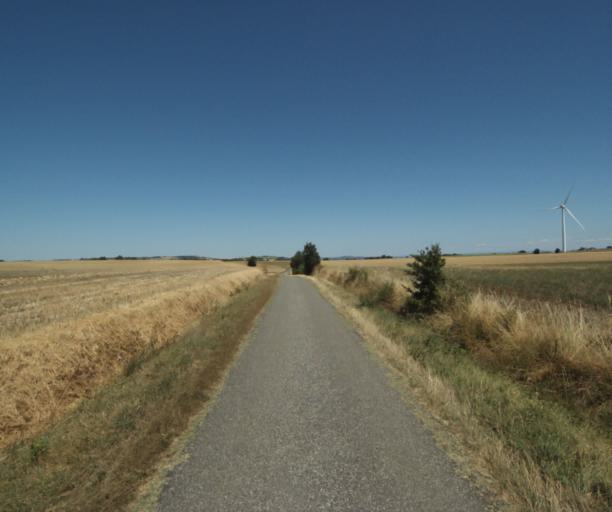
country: FR
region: Midi-Pyrenees
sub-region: Departement de la Haute-Garonne
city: Saint-Felix-Lauragais
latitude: 43.4690
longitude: 1.9101
